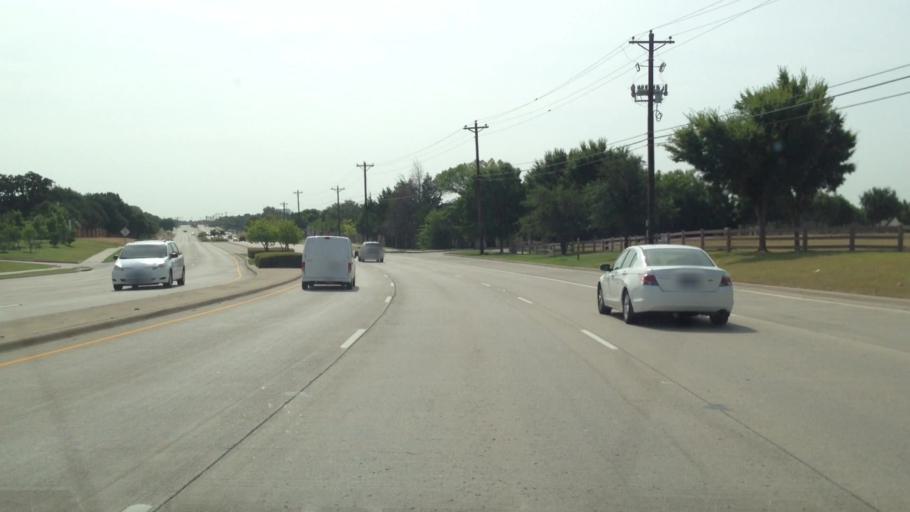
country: US
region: Texas
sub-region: Denton County
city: Flower Mound
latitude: 33.0101
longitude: -97.0442
